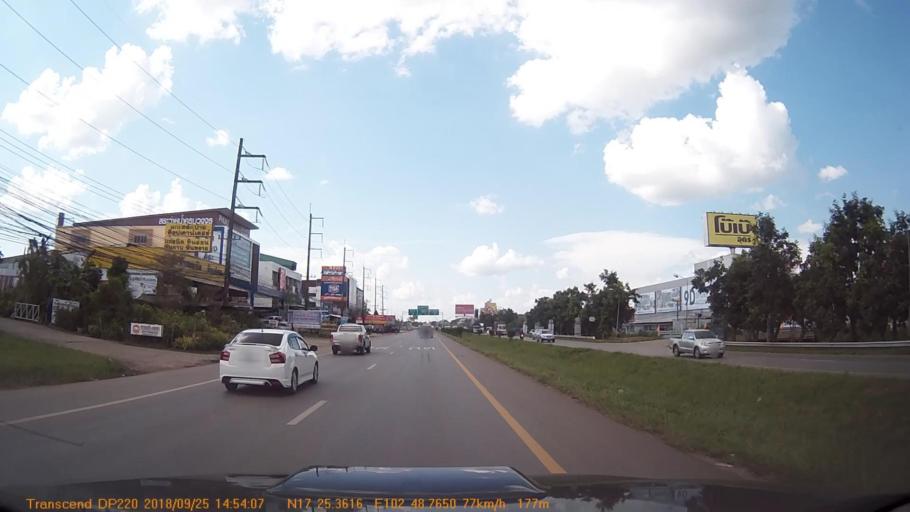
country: TH
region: Changwat Udon Thani
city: Udon Thani
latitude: 17.4232
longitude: 102.8125
